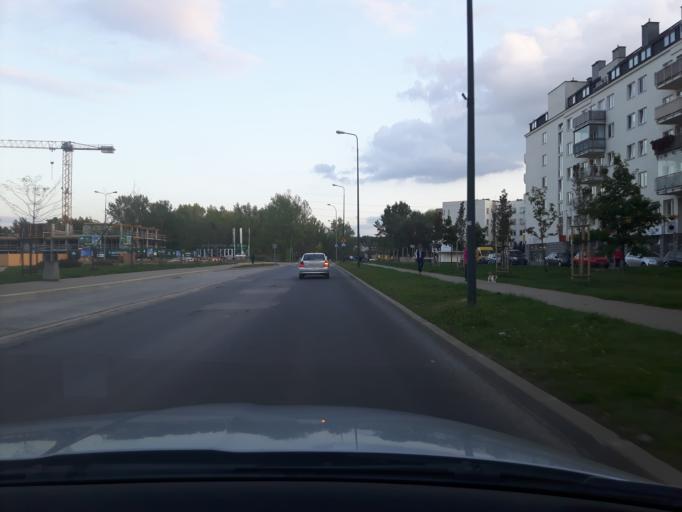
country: PL
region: Masovian Voivodeship
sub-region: Warszawa
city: Kabaty
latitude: 52.1290
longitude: 21.0679
